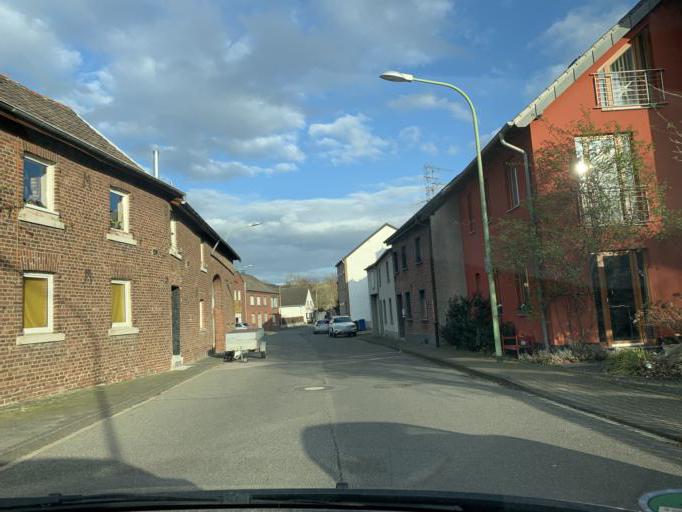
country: DE
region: North Rhine-Westphalia
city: Julich
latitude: 50.9234
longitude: 6.3987
